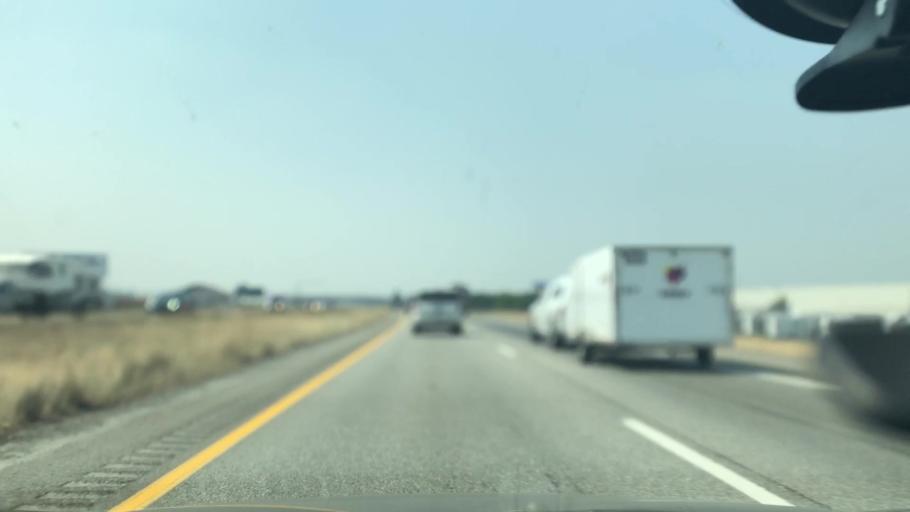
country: US
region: Idaho
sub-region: Kootenai County
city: Post Falls
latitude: 47.7124
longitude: -116.9060
